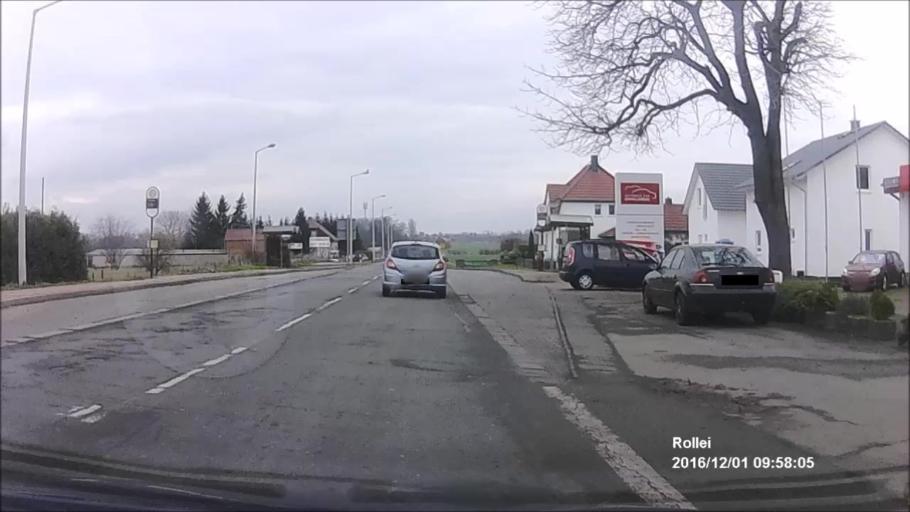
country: DE
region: Thuringia
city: Elxleben
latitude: 51.0332
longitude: 10.9685
